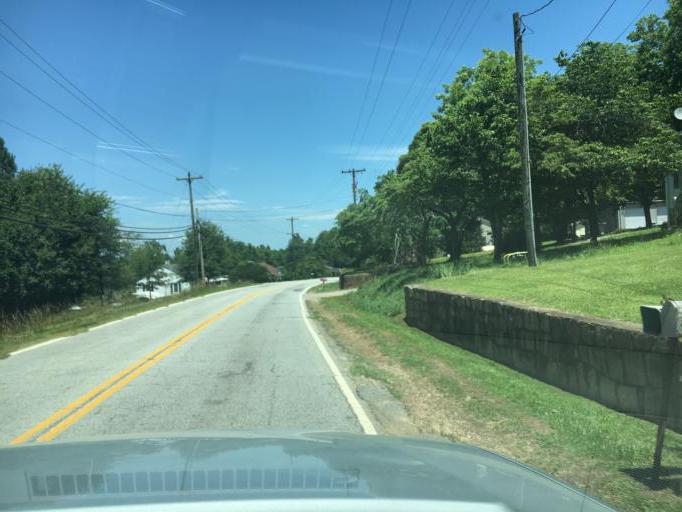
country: US
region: South Carolina
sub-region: Greenville County
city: Greer
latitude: 34.9513
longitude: -82.2126
